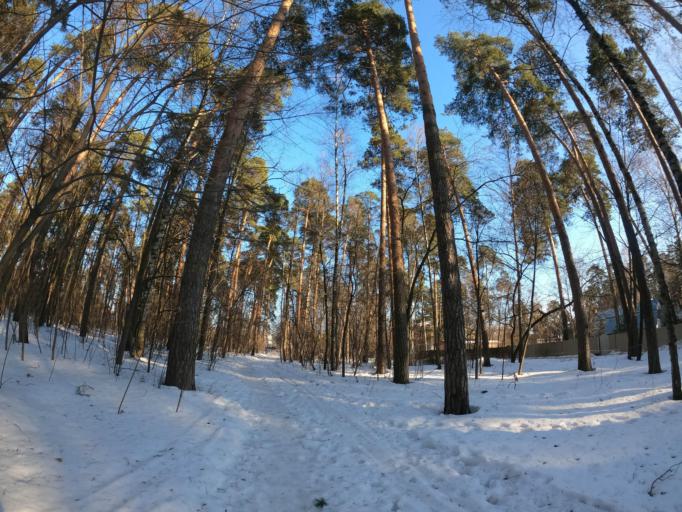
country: RU
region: Moskovskaya
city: Udel'naya
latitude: 55.6371
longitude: 38.0030
